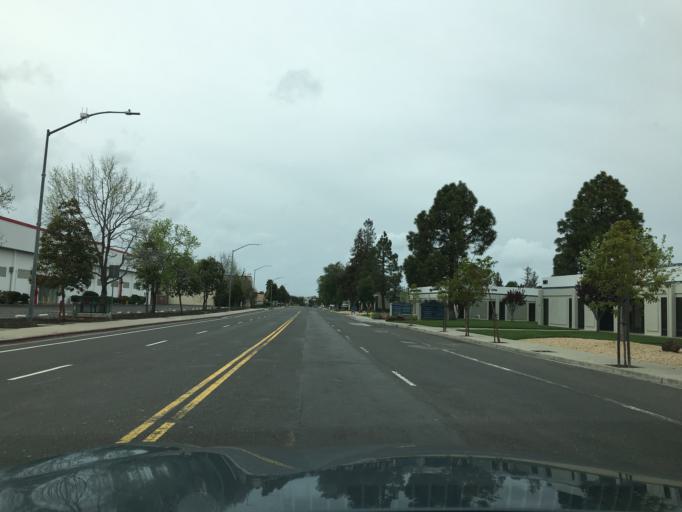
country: US
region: California
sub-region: San Mateo County
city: San Carlos
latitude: 37.5047
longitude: -122.2493
